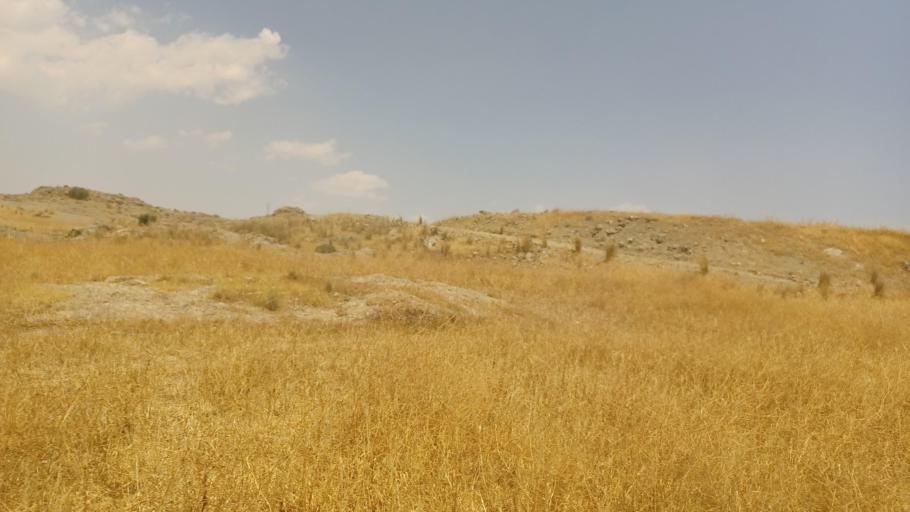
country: CY
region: Larnaka
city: Troulloi
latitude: 35.0189
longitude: 33.6042
